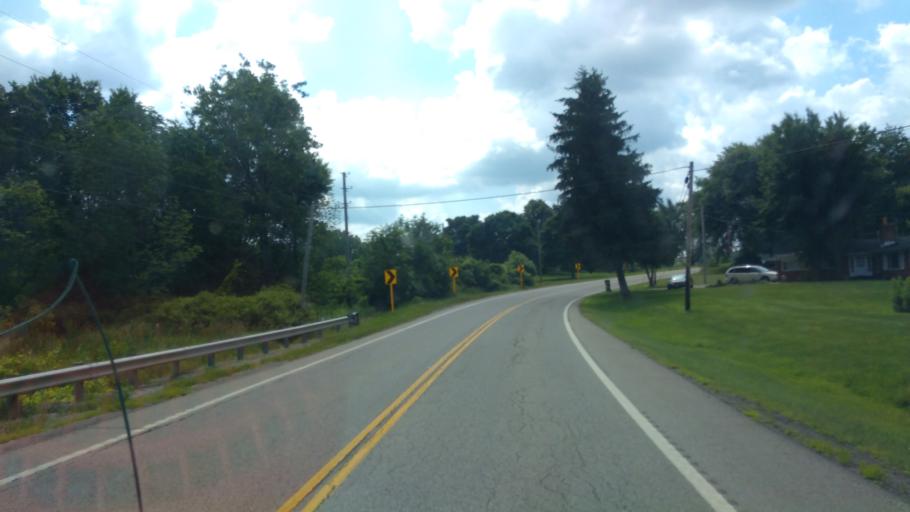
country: US
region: Ohio
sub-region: Richland County
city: Lincoln Heights
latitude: 40.7349
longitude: -82.4543
